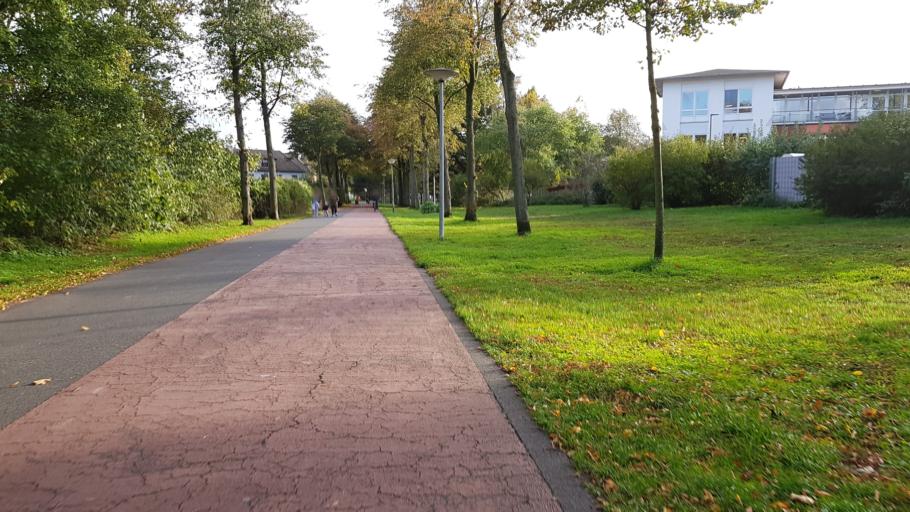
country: DE
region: Bremen
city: Bremen
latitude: 53.1117
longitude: 8.7612
